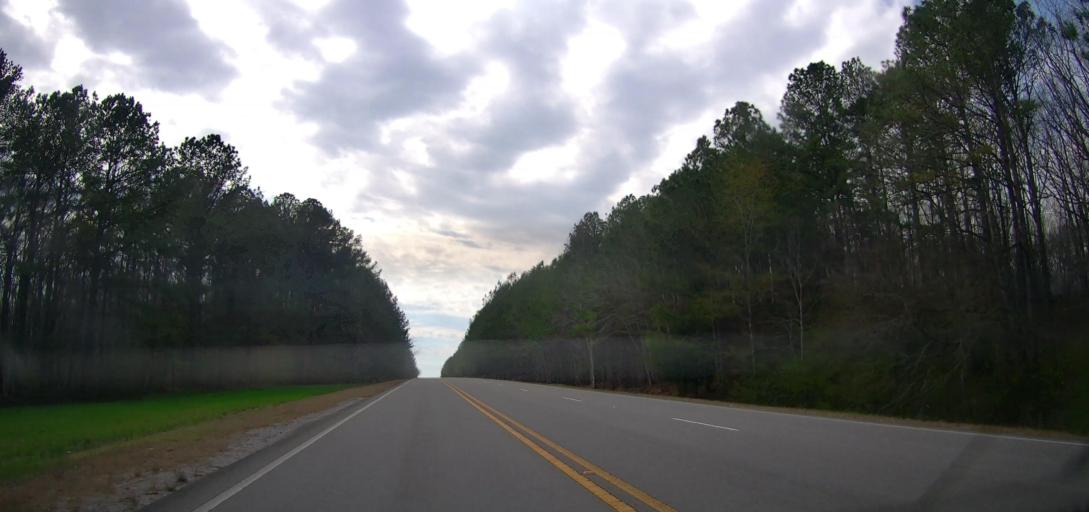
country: US
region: Alabama
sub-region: Marion County
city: Winfield
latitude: 33.9319
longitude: -87.7437
